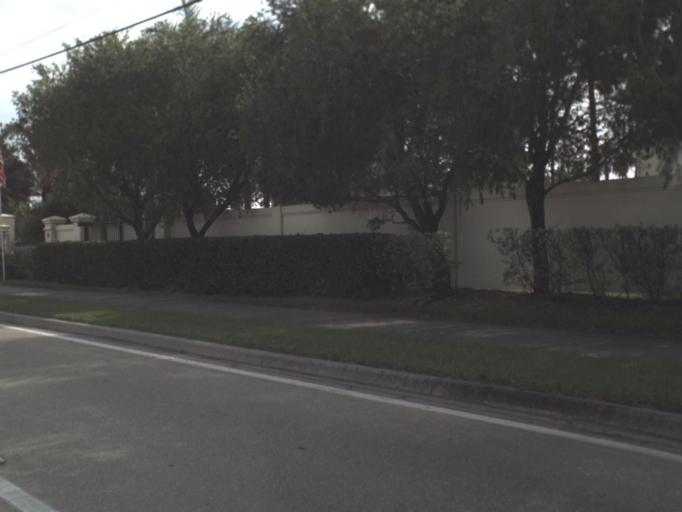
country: US
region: Florida
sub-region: Lee County
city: Cypress Lake
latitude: 26.5400
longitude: -81.9176
